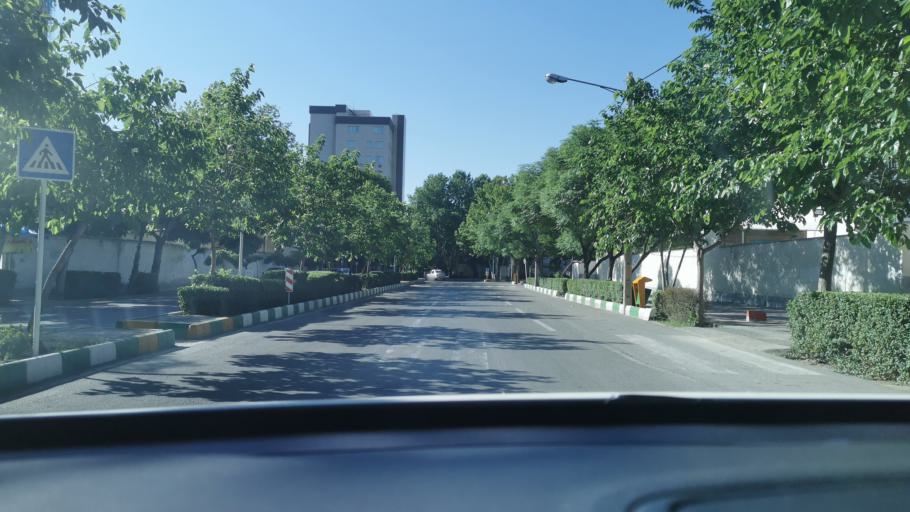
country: IR
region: Razavi Khorasan
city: Mashhad
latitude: 36.2878
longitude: 59.5735
